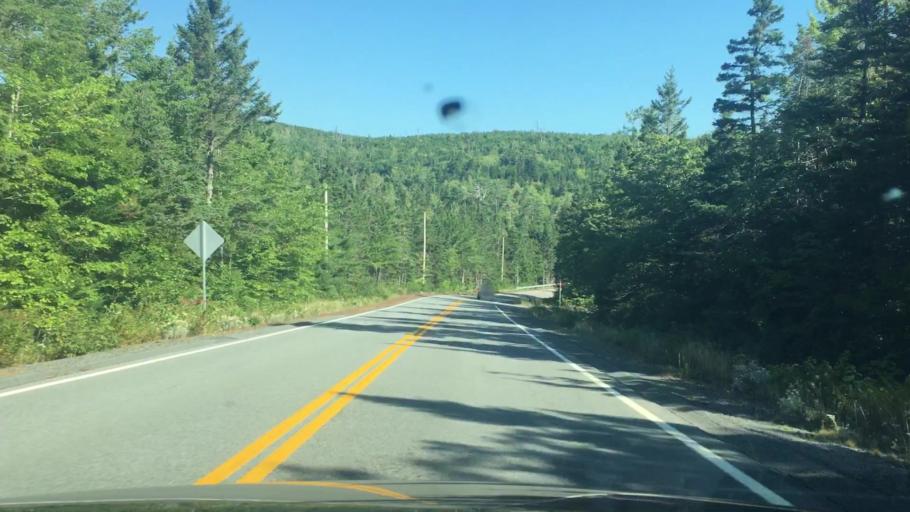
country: CA
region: Nova Scotia
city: Cole Harbour
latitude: 44.8139
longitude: -62.8858
